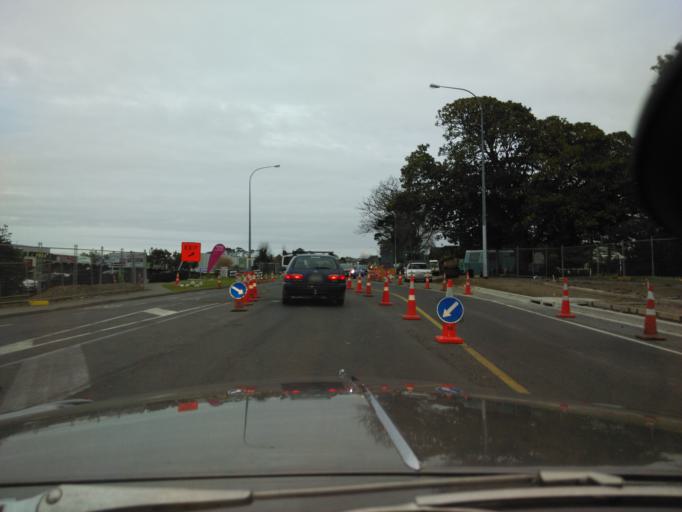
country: NZ
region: Auckland
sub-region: Auckland
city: Rothesay Bay
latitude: -36.7434
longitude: 174.6928
